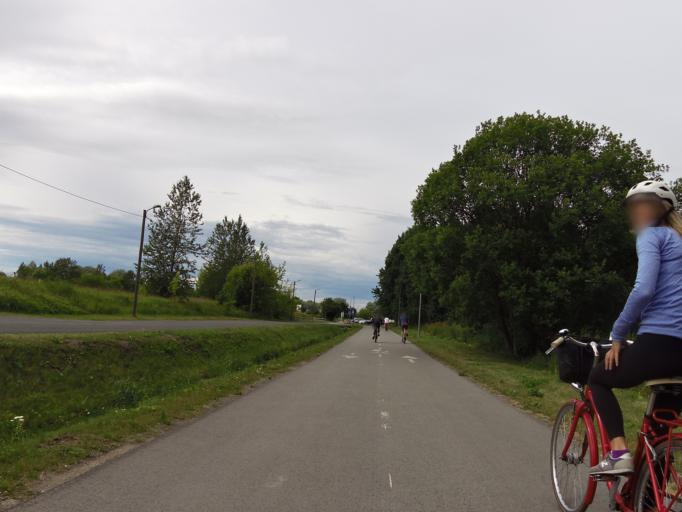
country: EE
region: Harju
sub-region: Tallinna linn
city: Tallinn
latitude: 59.4336
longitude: 24.6851
